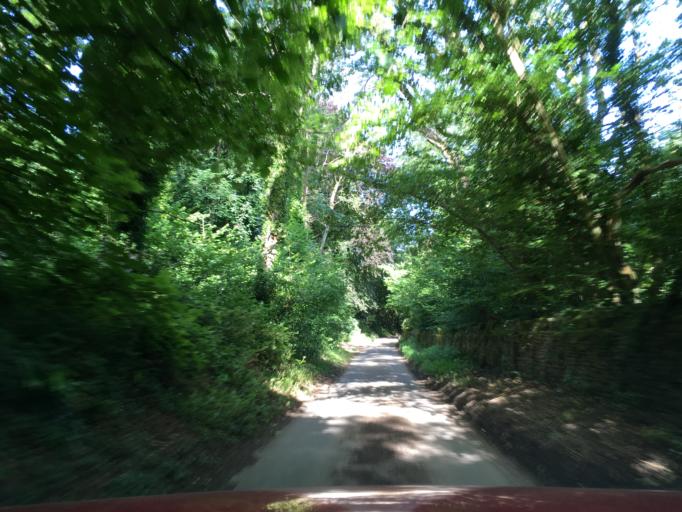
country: GB
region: England
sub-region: Wiltshire
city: Nettleton
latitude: 51.4928
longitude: -2.2692
